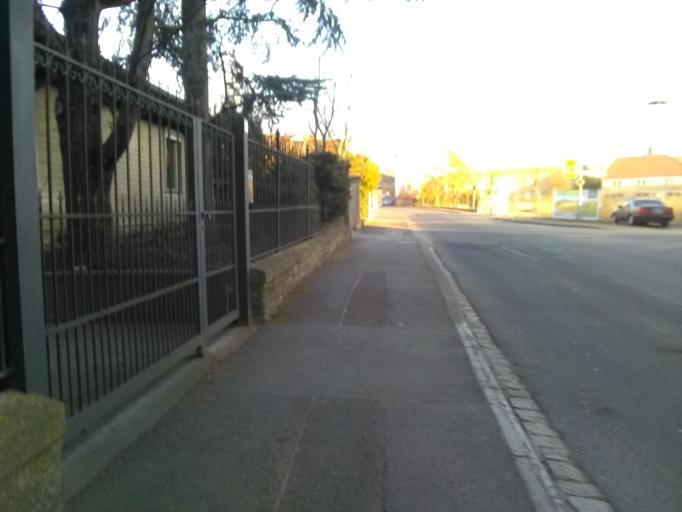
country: DE
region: Bavaria
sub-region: Regierungsbezirk Unterfranken
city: Kitzingen
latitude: 49.7339
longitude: 10.1651
